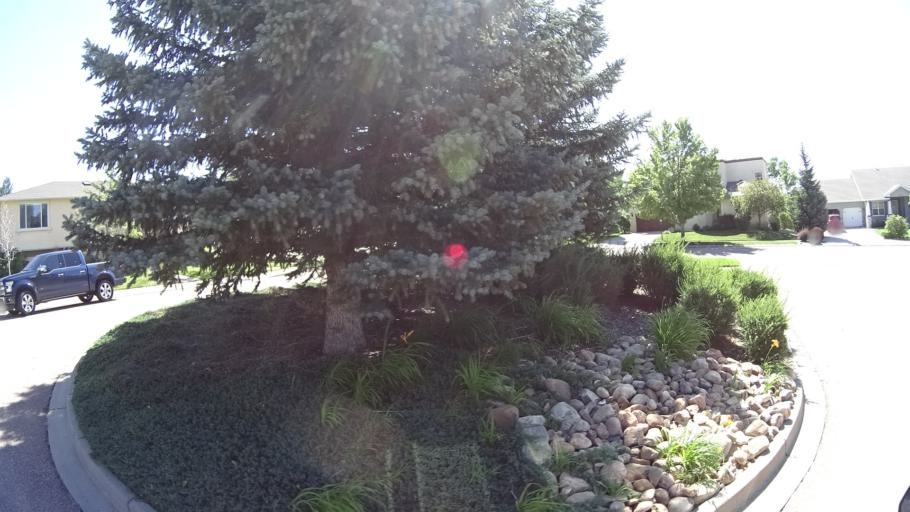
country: US
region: Colorado
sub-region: El Paso County
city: Black Forest
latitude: 38.9749
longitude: -104.7747
